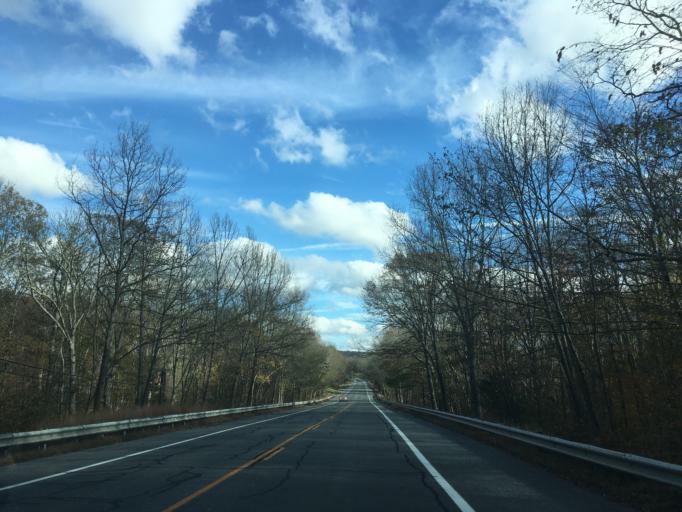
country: US
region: Rhode Island
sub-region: Providence County
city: Foster
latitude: 41.8465
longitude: -71.7029
